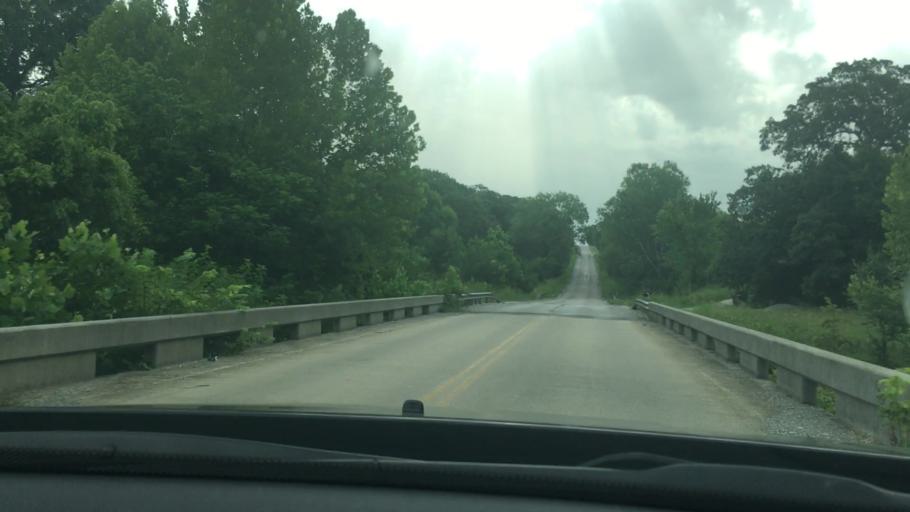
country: US
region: Oklahoma
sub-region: Pontotoc County
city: Ada
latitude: 34.8107
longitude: -96.6442
